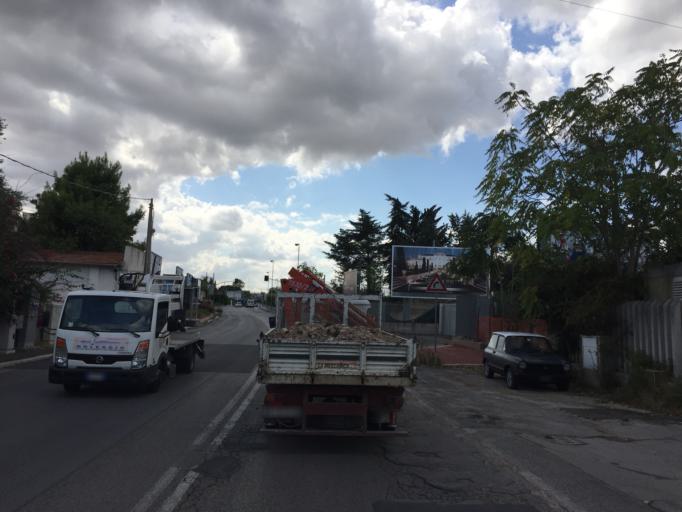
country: IT
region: Apulia
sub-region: Provincia di Bari
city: Bari
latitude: 41.0932
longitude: 16.8833
